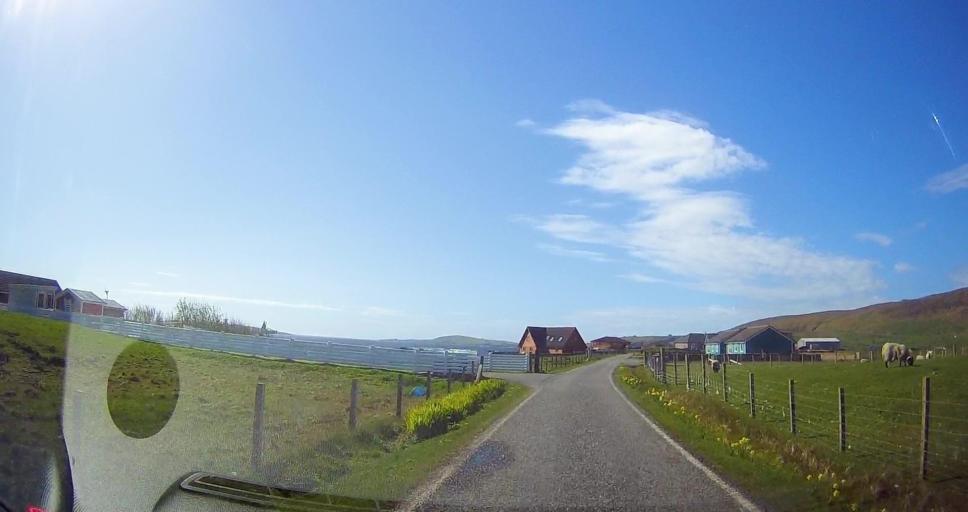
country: GB
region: Scotland
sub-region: Shetland Islands
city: Sandwick
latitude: 60.0379
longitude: -1.2178
